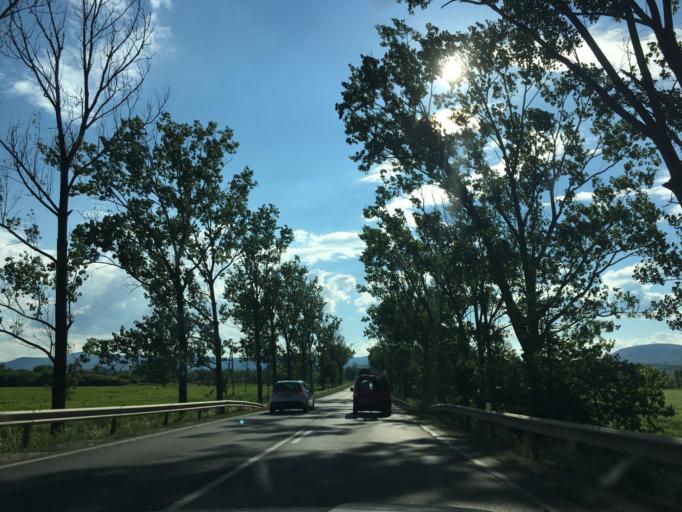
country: HU
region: Borsod-Abauj-Zemplen
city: Tolcsva
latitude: 48.2644
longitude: 21.4636
